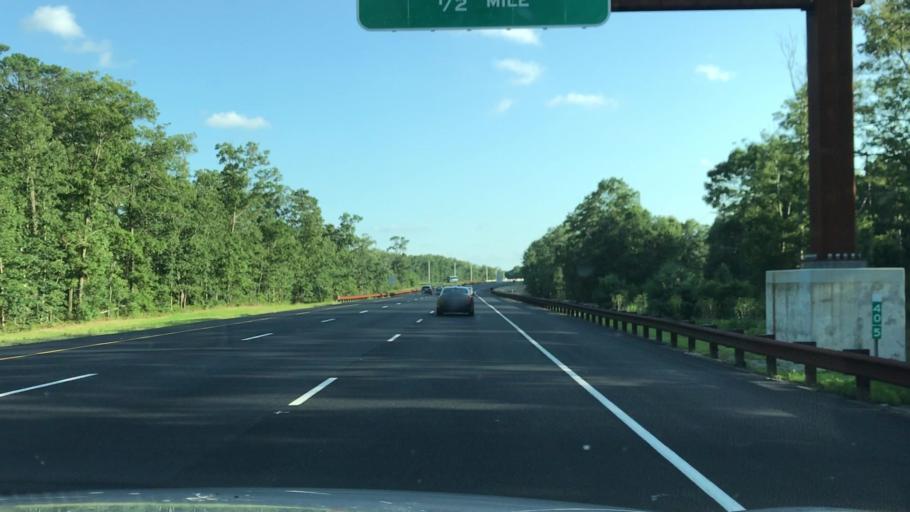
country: US
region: New Jersey
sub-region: Atlantic County
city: Pomona
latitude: 39.4584
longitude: -74.5348
